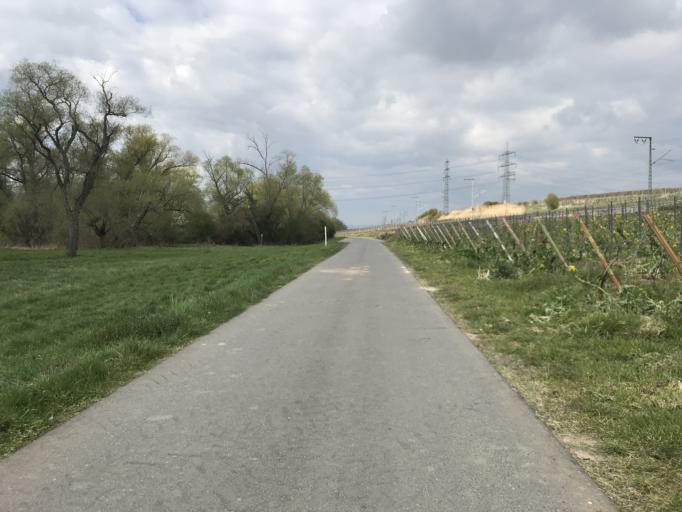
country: DE
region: Hesse
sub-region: Regierungsbezirk Darmstadt
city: Bischofsheim
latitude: 50.0003
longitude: 8.3883
